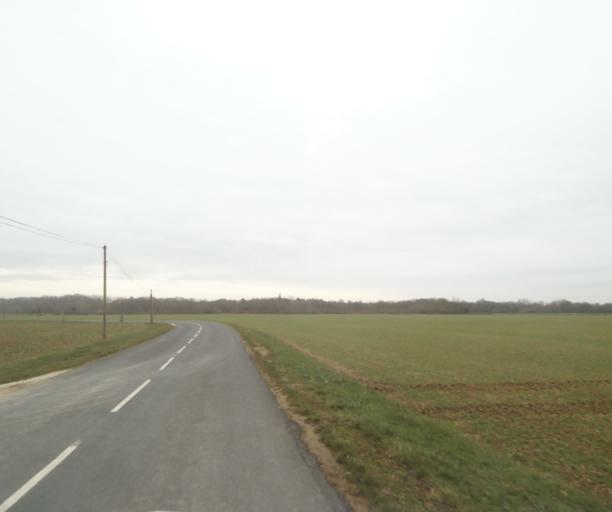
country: FR
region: Champagne-Ardenne
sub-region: Departement de la Haute-Marne
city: Villiers-en-Lieu
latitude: 48.6463
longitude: 4.7624
